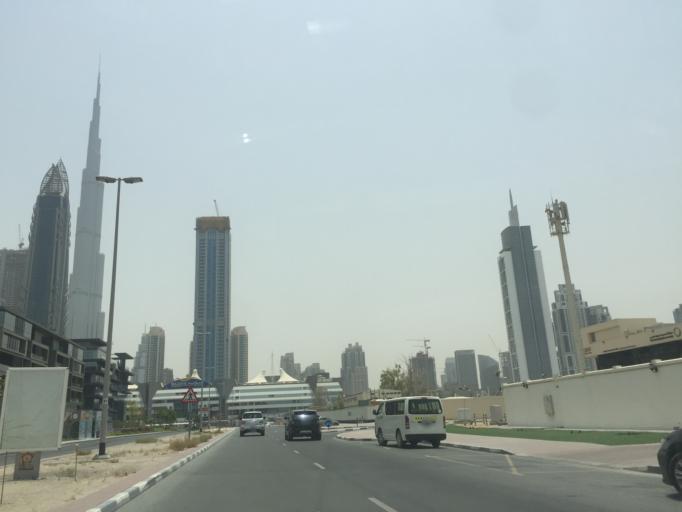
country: AE
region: Dubai
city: Dubai
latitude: 25.2007
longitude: 55.2621
